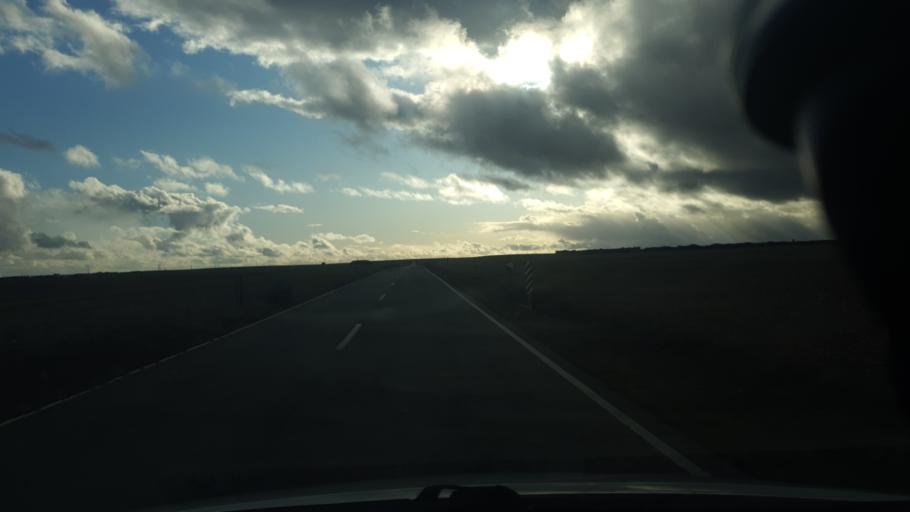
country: ES
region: Castille and Leon
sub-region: Provincia de Segovia
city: Santiuste de San Juan Bautista
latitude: 41.1405
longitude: -4.5907
